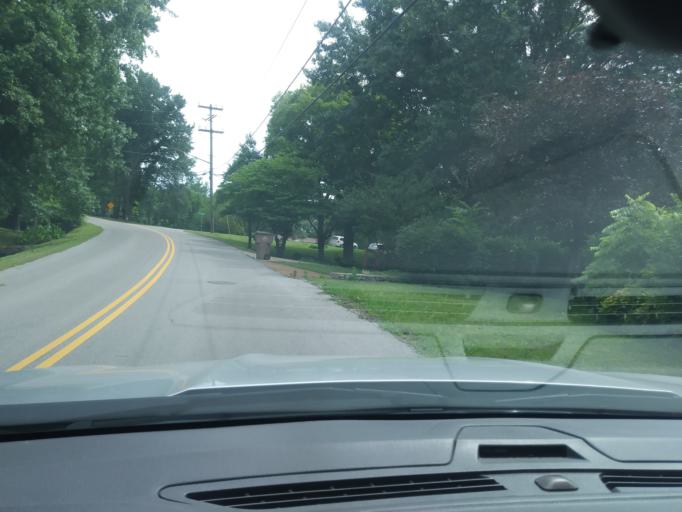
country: US
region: Tennessee
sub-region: Davidson County
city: Oak Hill
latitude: 36.1266
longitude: -86.7208
